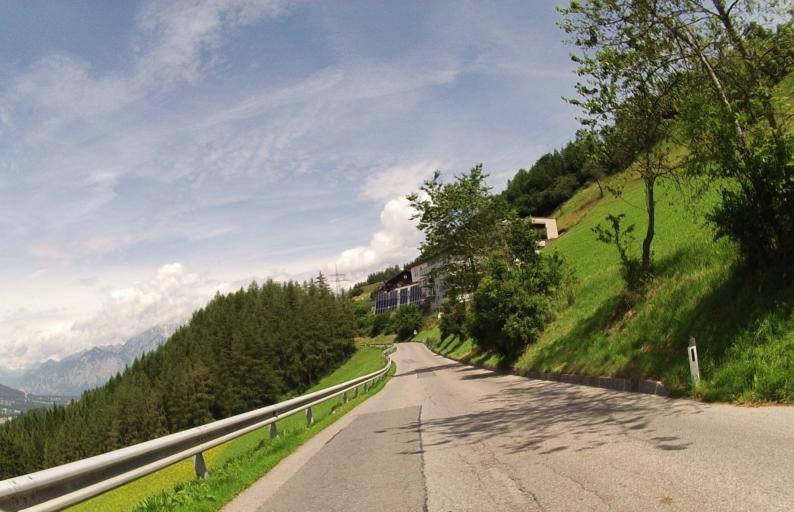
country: AT
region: Tyrol
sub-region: Politischer Bezirk Innsbruck Land
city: Schoenberg im Stubaital
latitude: 47.1911
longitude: 11.4275
